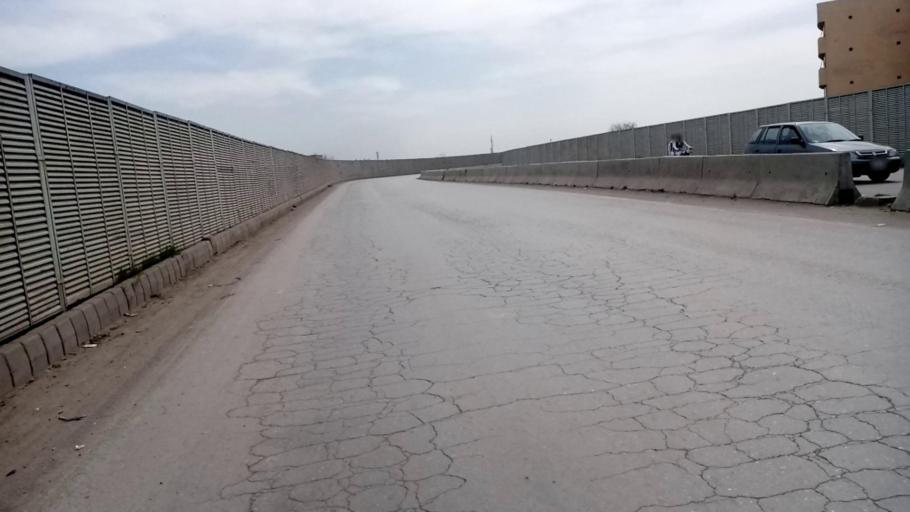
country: PK
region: Khyber Pakhtunkhwa
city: Peshawar
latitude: 34.0186
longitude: 71.6495
